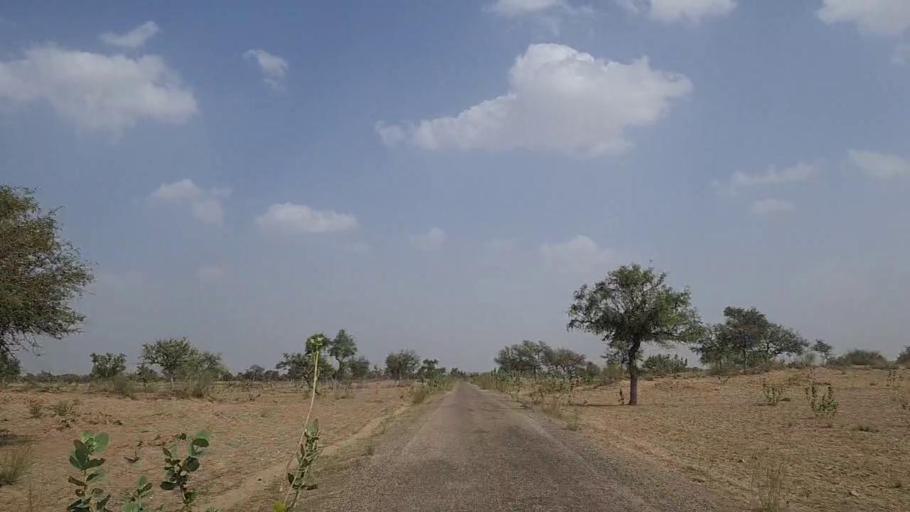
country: PK
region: Sindh
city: Islamkot
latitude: 24.8299
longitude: 70.1599
